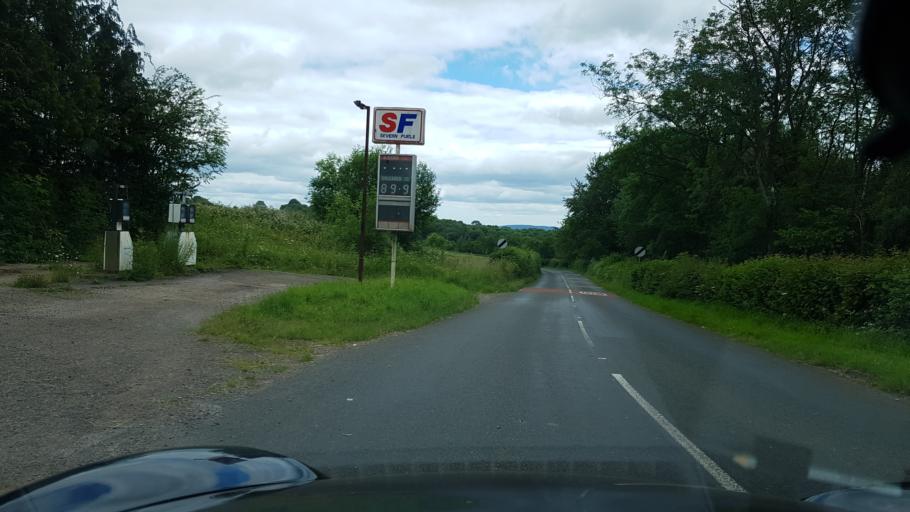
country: GB
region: Wales
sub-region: Monmouthshire
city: Grosmont
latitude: 51.8732
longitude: -2.8623
